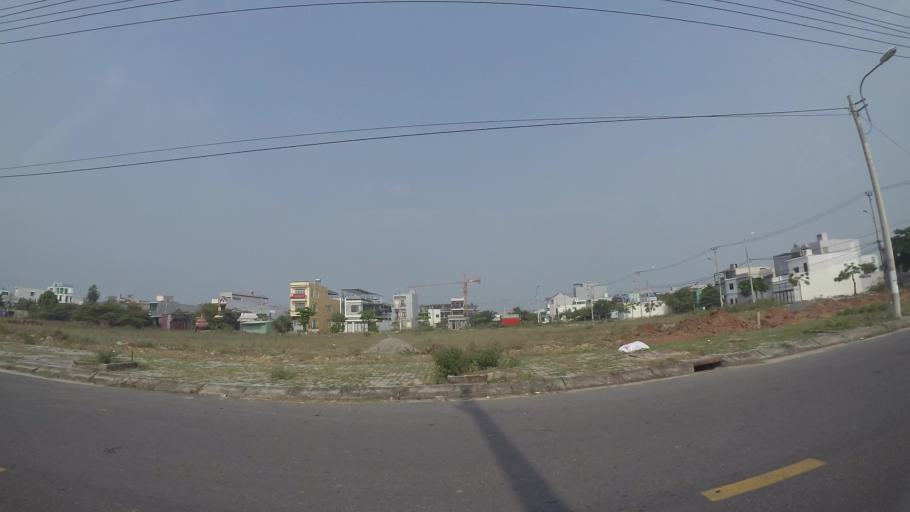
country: VN
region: Da Nang
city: Cam Le
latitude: 16.0020
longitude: 108.2236
